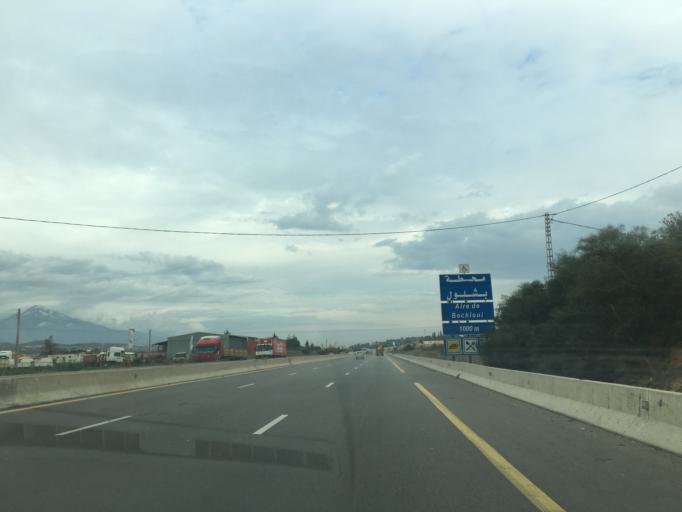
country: DZ
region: Bouira
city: Bouira
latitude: 36.3114
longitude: 4.0458
